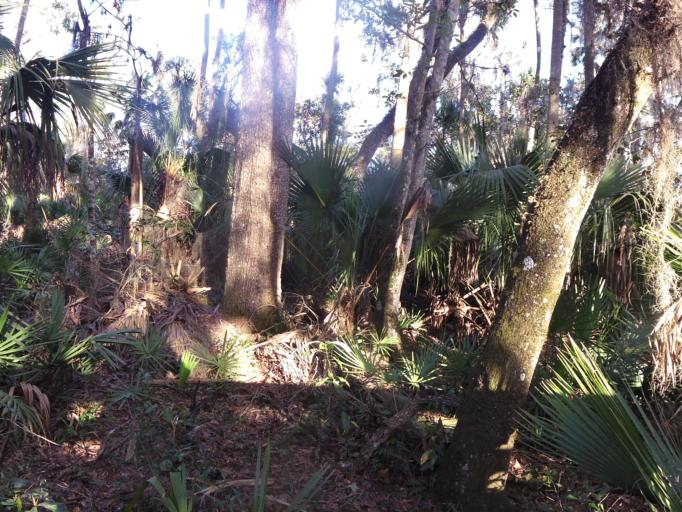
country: US
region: Florida
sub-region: Volusia County
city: Orange City
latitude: 28.9467
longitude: -81.3389
